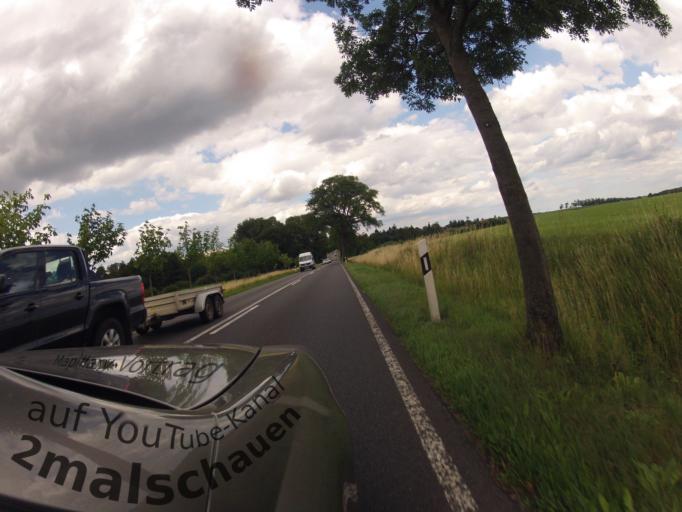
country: DE
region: Mecklenburg-Vorpommern
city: Anklam
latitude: 53.9016
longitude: 13.7378
